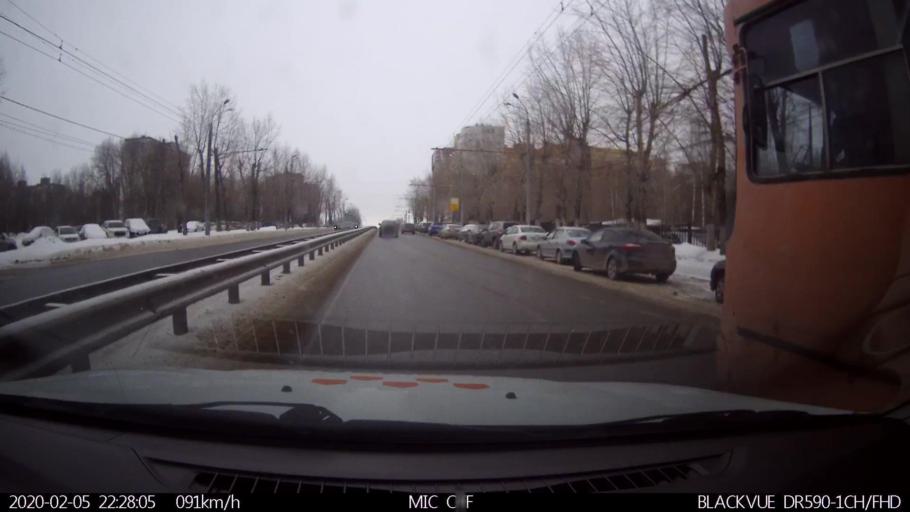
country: RU
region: Nizjnij Novgorod
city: Imeni Stepana Razina
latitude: 54.7602
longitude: 44.1266
